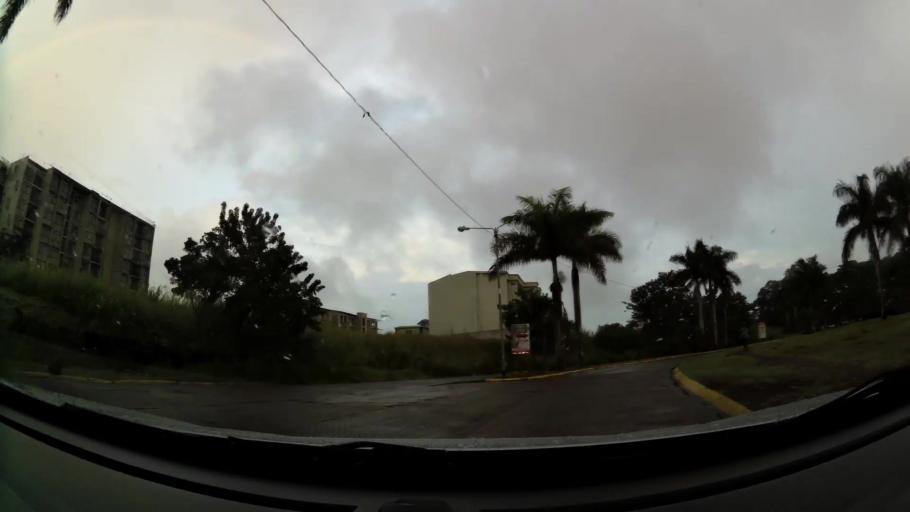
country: CR
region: Heredia
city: La Asuncion
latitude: 9.9795
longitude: -84.1579
